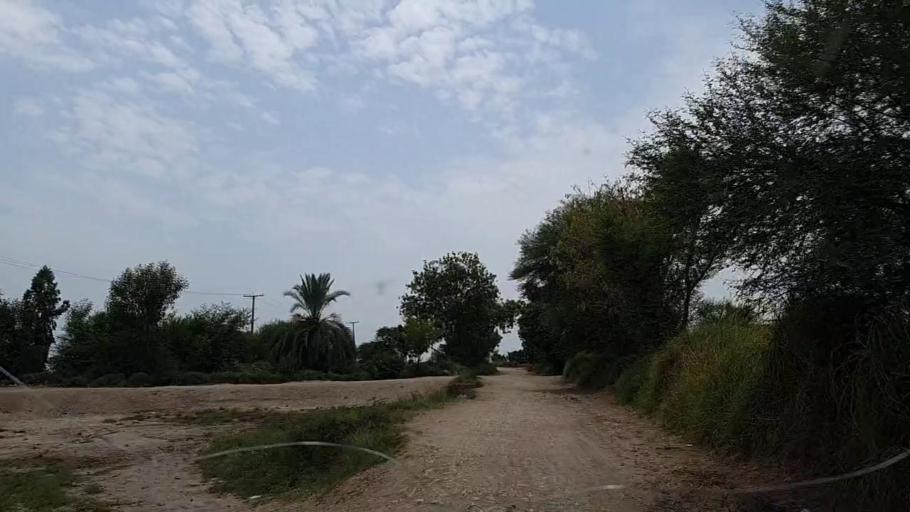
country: PK
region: Sindh
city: Tharu Shah
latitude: 26.9247
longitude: 68.0830
